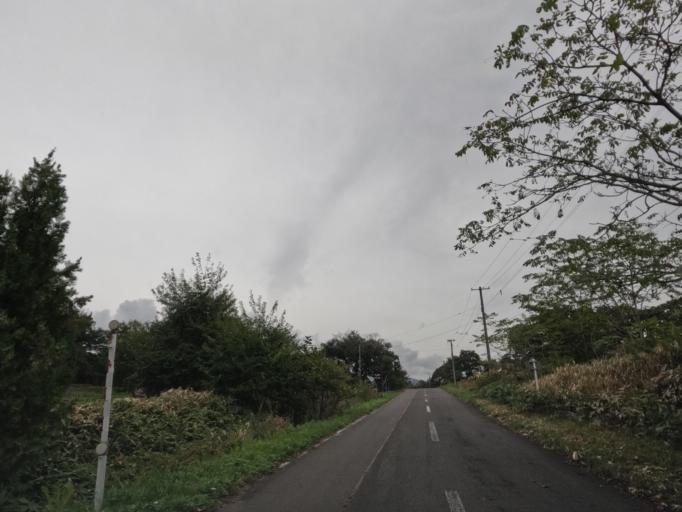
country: JP
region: Hokkaido
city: Date
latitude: 42.4050
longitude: 140.9166
